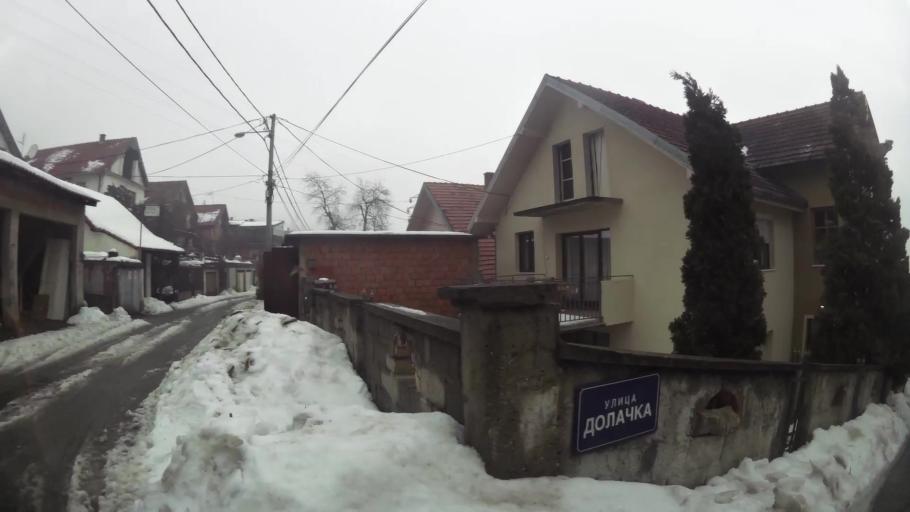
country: RS
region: Central Serbia
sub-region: Belgrade
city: Zvezdara
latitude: 44.7850
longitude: 20.5247
